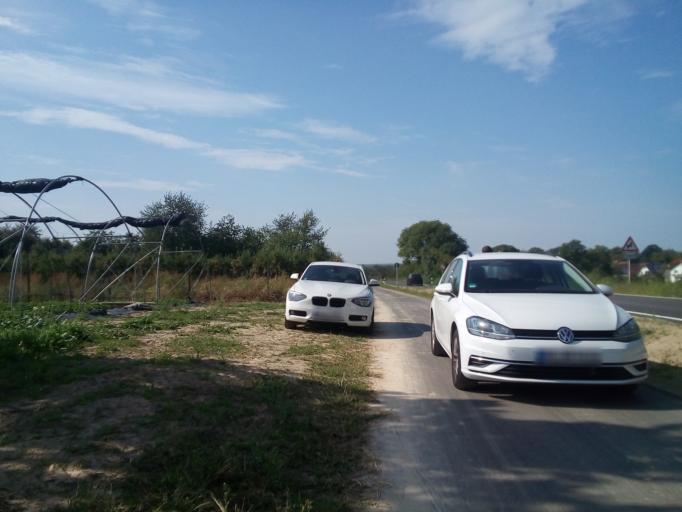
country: DE
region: Baden-Wuerttemberg
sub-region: Freiburg Region
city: Lauf
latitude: 48.6546
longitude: 8.1224
